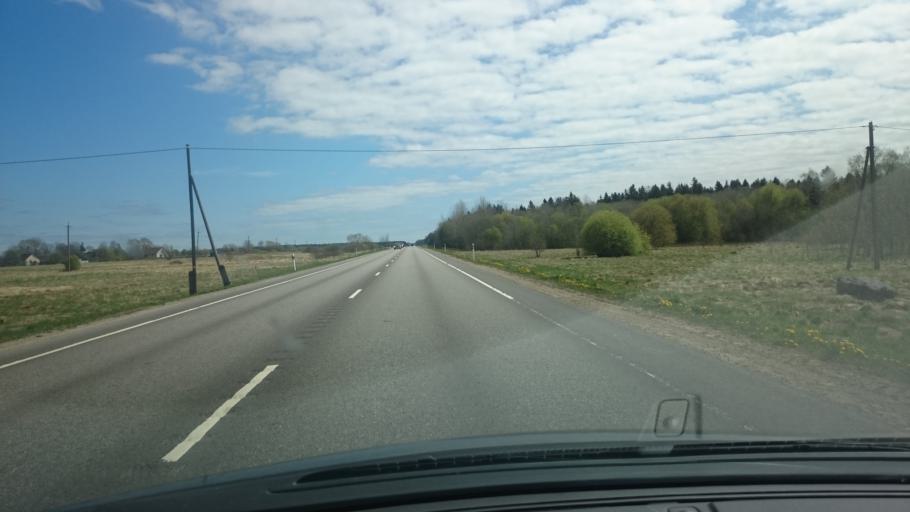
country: EE
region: Ida-Virumaa
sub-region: Kohtla-Jaerve linn
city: Kohtla-Jarve
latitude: 59.4210
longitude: 27.2085
